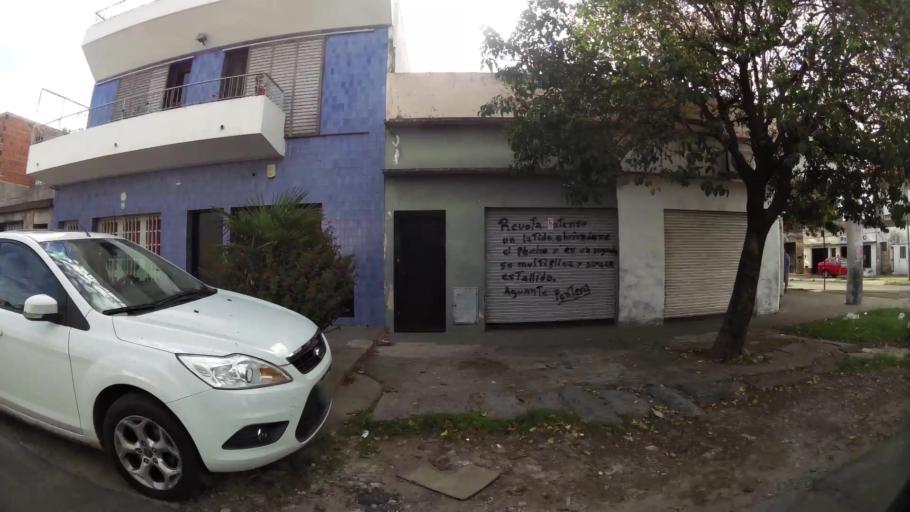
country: AR
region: Santa Fe
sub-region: Departamento de Rosario
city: Rosario
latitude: -32.9758
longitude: -60.6785
